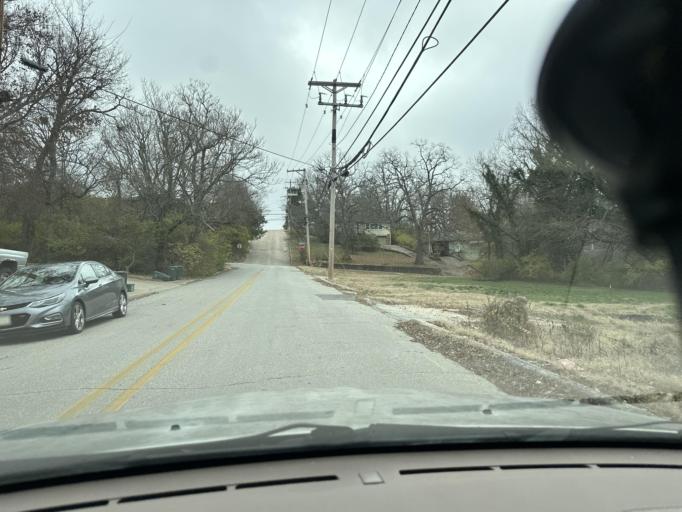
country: US
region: Arkansas
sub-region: Washington County
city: Fayetteville
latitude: 36.0609
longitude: -94.1639
